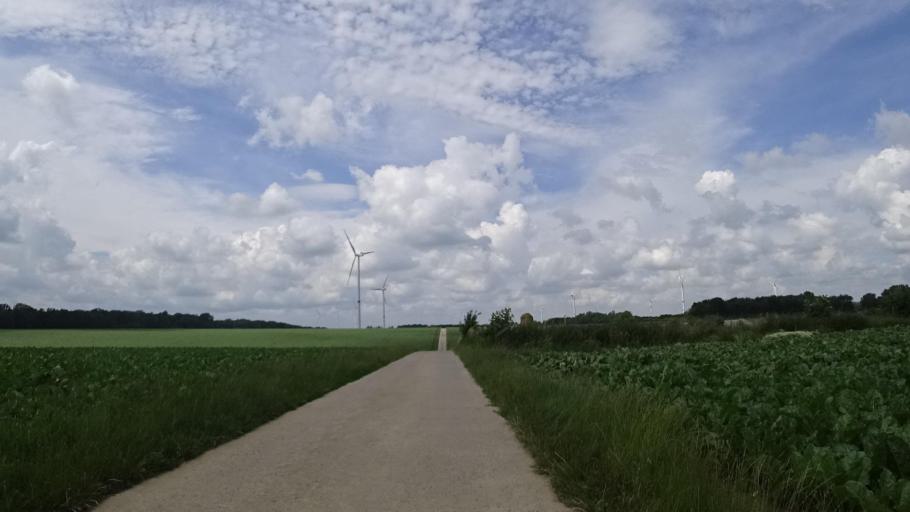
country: BE
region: Wallonia
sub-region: Province du Brabant Wallon
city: Perwez
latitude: 50.5857
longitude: 4.7979
